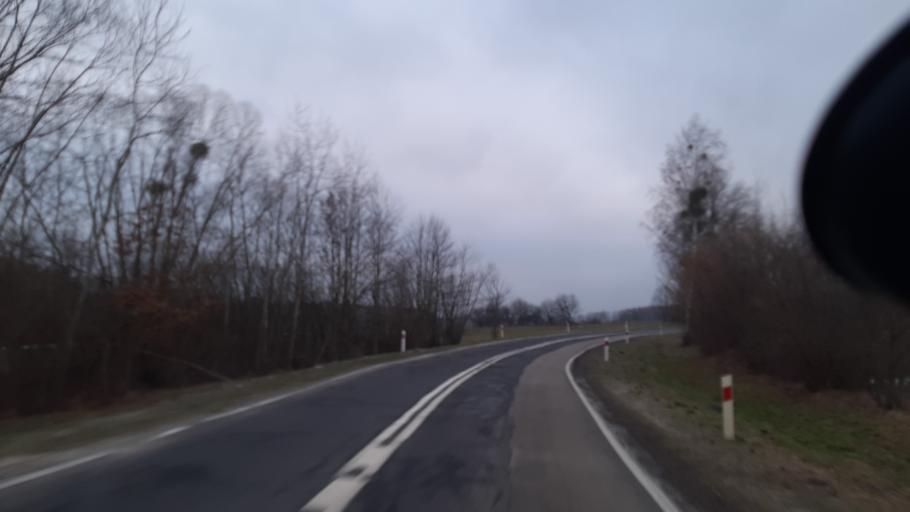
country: PL
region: Lublin Voivodeship
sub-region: Powiat parczewski
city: Podedworze
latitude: 51.5750
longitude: 23.2221
